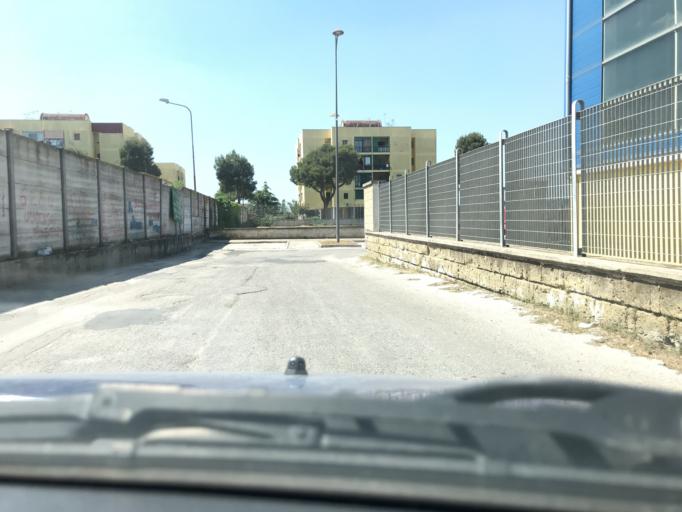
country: IT
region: Campania
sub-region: Provincia di Napoli
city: Villaricca
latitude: 40.9165
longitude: 14.1769
